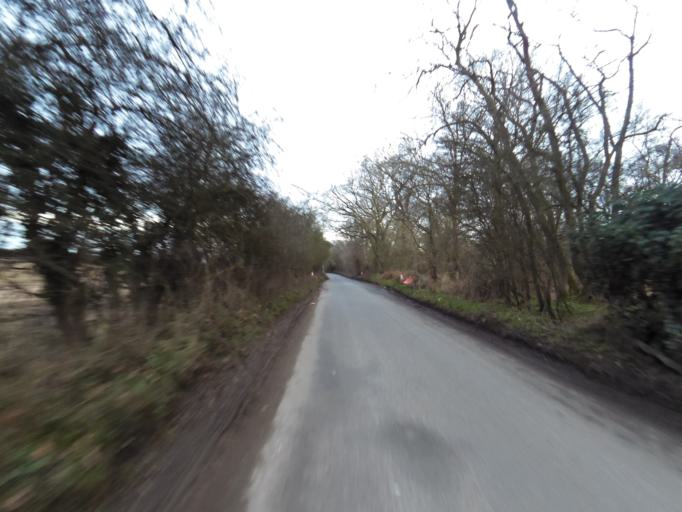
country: GB
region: England
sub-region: Suffolk
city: Ipswich
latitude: 52.0198
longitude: 1.1142
